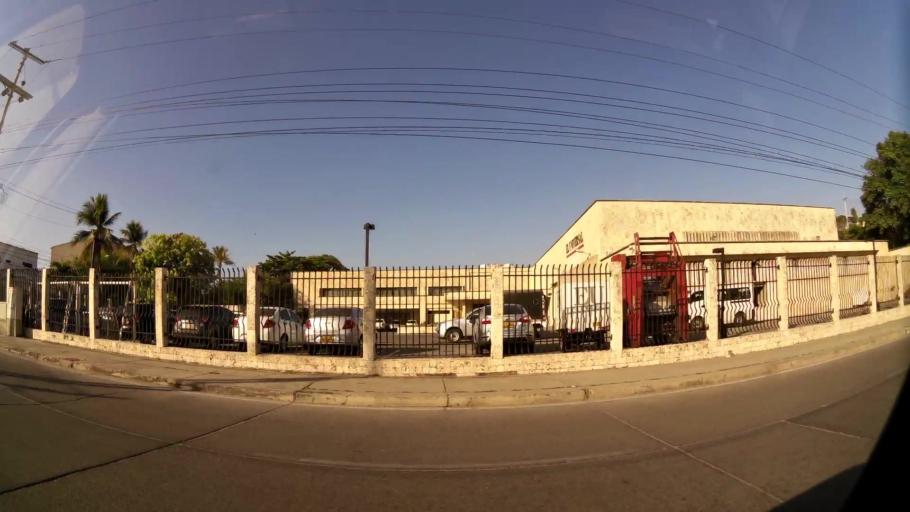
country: CO
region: Bolivar
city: Cartagena
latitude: 10.4199
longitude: -75.5404
